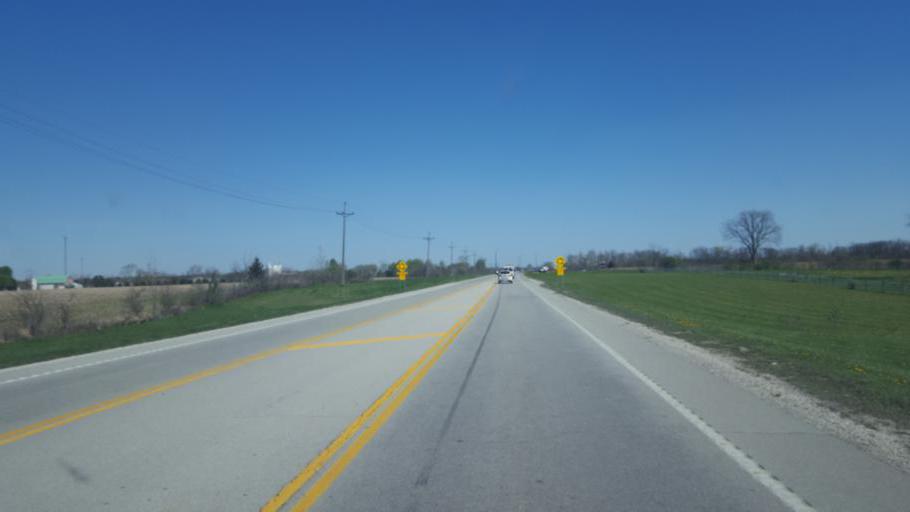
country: US
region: Ohio
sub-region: Sandusky County
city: Stony Prairie
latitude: 41.3502
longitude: -83.1654
